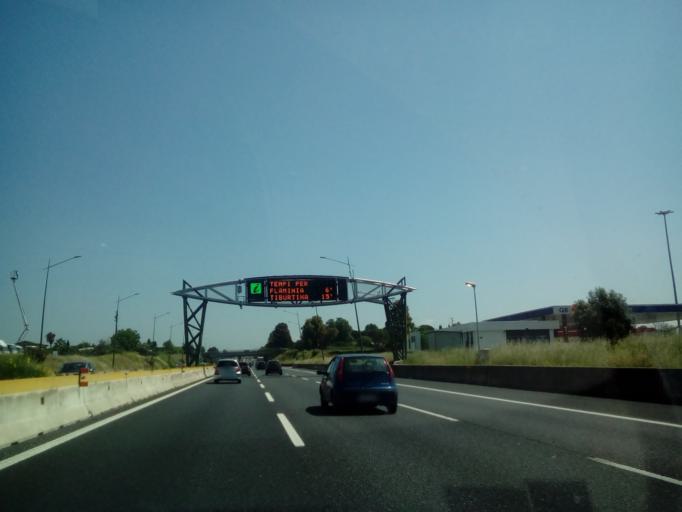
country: IT
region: Latium
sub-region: Citta metropolitana di Roma Capitale
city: Valle Santa
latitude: 41.9590
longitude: 12.3882
